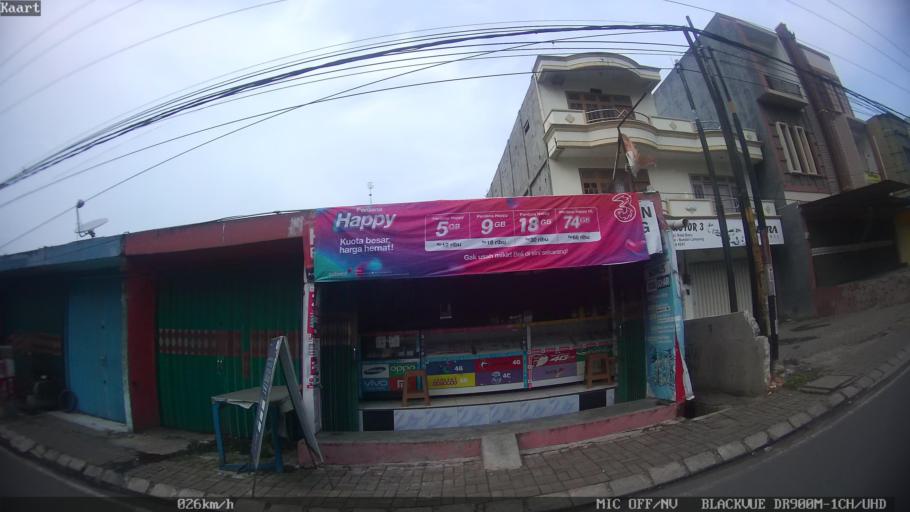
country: ID
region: Lampung
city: Bandarlampung
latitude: -5.4190
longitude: 105.2690
